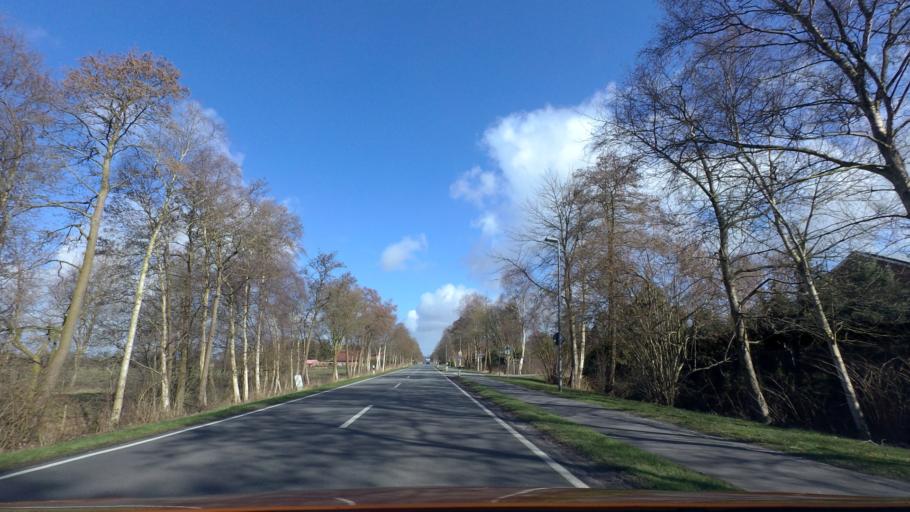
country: DE
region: Lower Saxony
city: Edewecht
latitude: 53.0907
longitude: 7.9426
